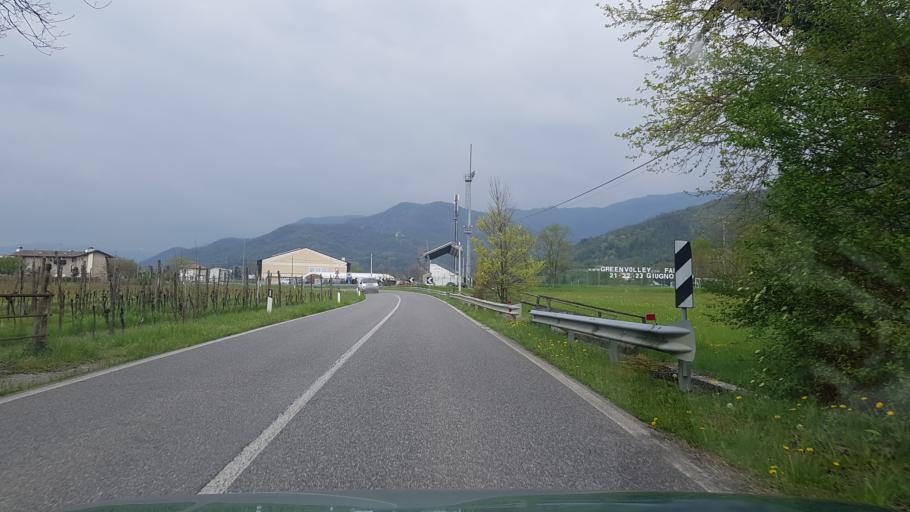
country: IT
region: Friuli Venezia Giulia
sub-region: Provincia di Udine
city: Faedis
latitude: 46.1380
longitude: 13.3507
